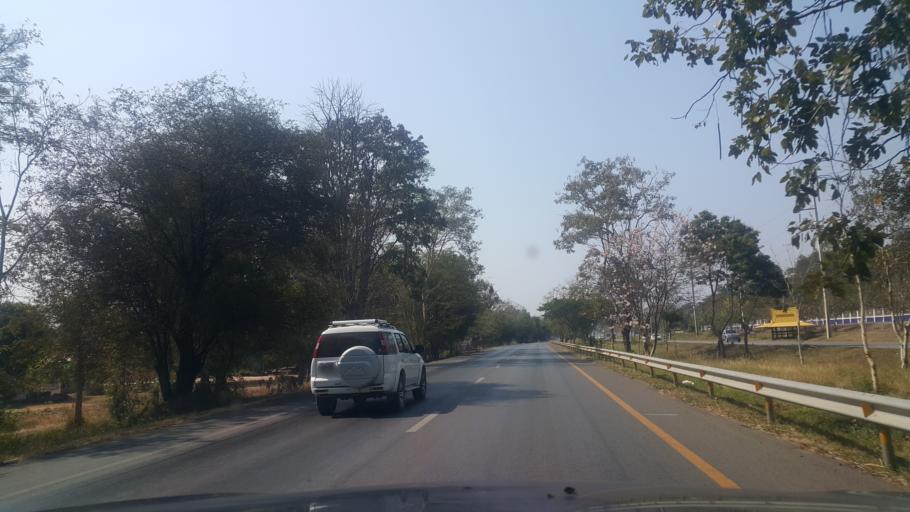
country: TH
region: Nakhon Ratchasima
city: Pak Thong Chai
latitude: 14.5944
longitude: 102.0022
